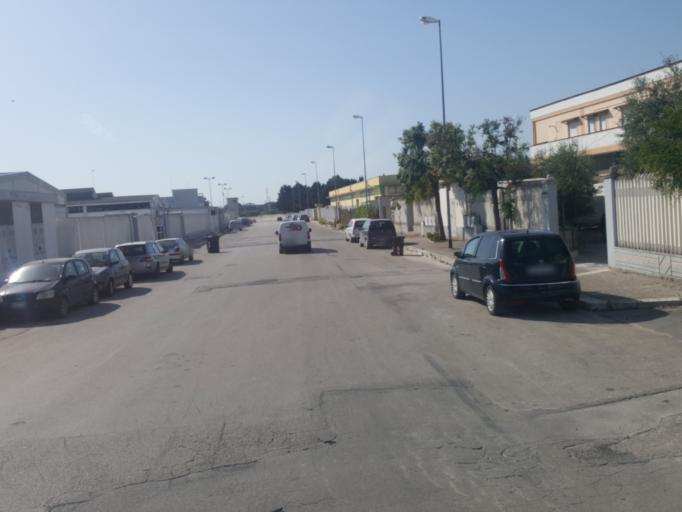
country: IT
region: Apulia
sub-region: Provincia di Barletta - Andria - Trani
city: Barletta
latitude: 41.3094
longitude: 16.3044
